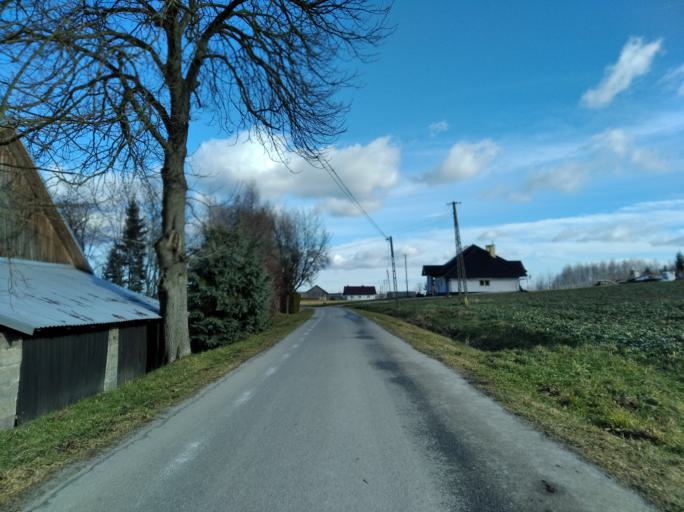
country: PL
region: Subcarpathian Voivodeship
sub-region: Powiat strzyzowski
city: Wisniowa
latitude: 49.8976
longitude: 21.6960
